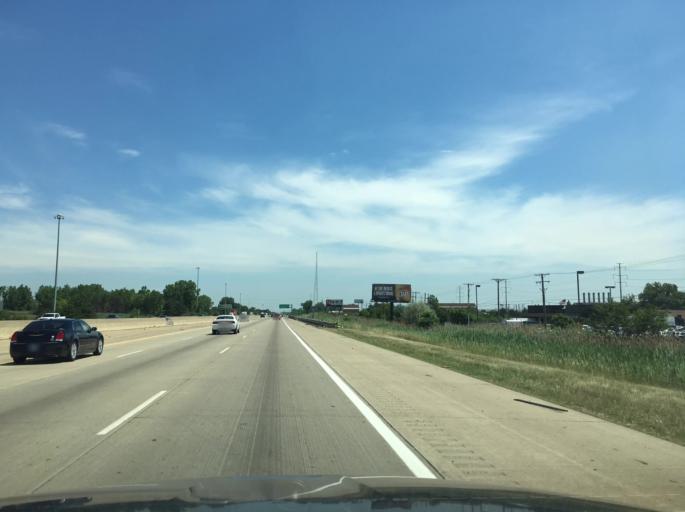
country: US
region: Michigan
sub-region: Wayne County
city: Melvindale
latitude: 42.2931
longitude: -83.1892
